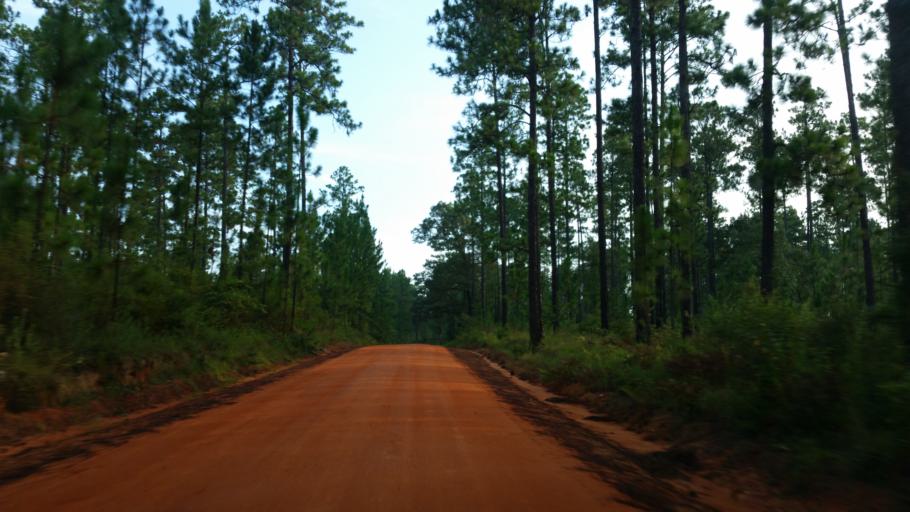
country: US
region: Alabama
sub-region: Escambia County
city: Atmore
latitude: 30.8804
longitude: -87.5827
